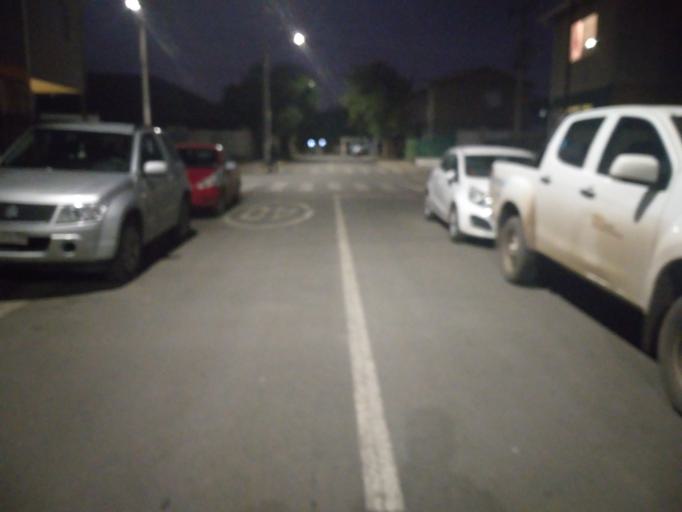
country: CL
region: Valparaiso
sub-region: Provincia de Quillota
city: Hacienda La Calera
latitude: -32.7945
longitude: -71.2227
